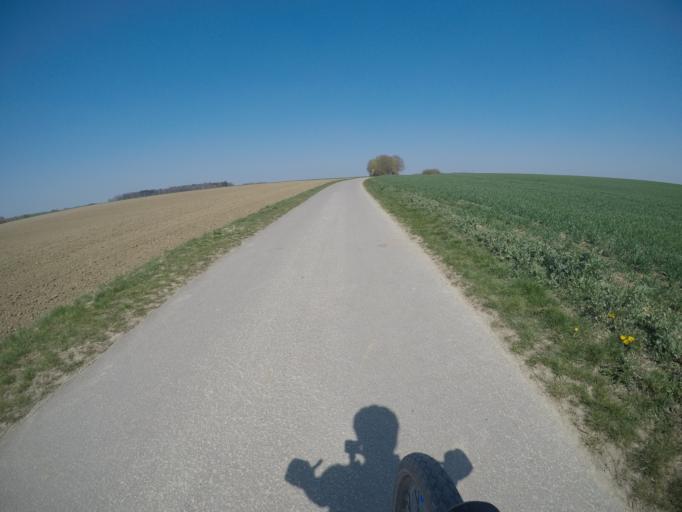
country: DE
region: Baden-Wuerttemberg
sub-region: Regierungsbezirk Stuttgart
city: Renningen
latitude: 48.7378
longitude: 8.9224
